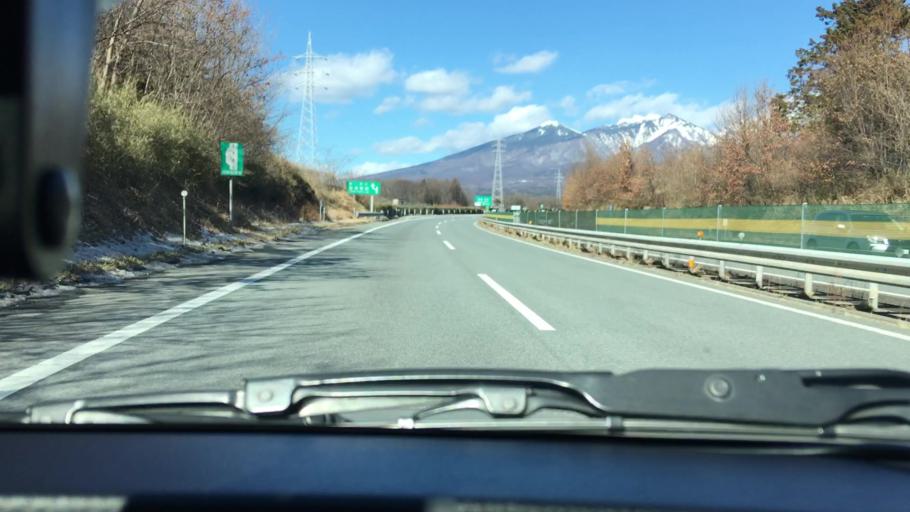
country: JP
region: Yamanashi
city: Nirasaki
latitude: 35.8250
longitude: 138.3934
